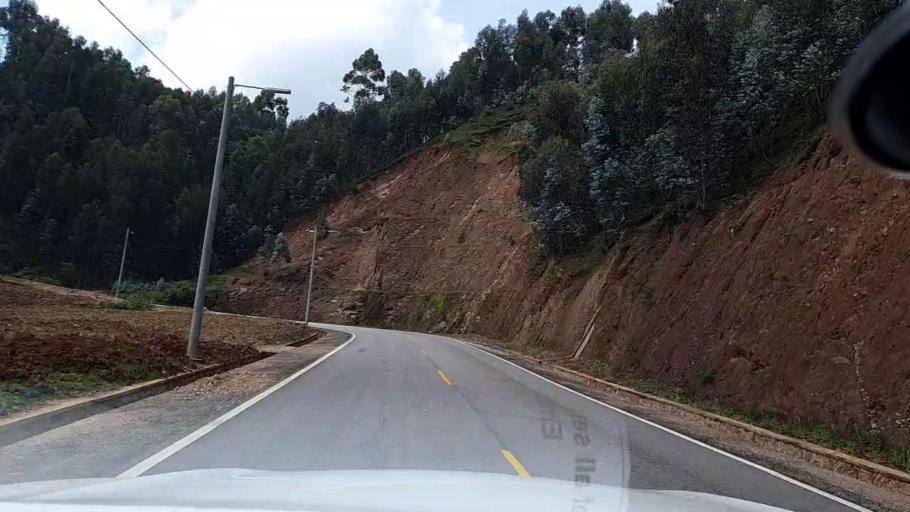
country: RW
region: Southern Province
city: Nzega
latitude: -2.5118
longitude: 29.4622
